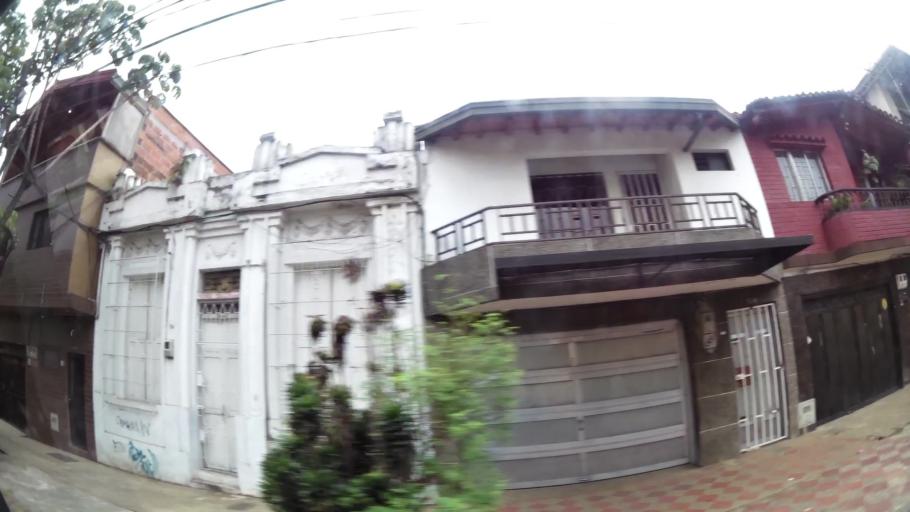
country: CO
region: Antioquia
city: Medellin
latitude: 6.2474
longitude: -75.5549
